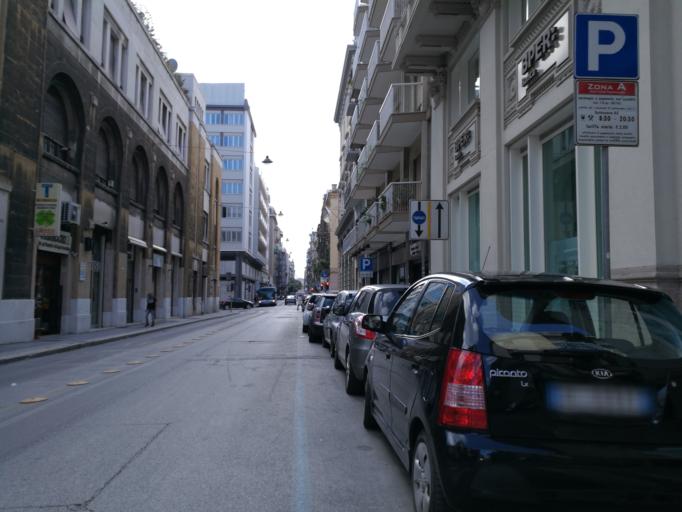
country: IT
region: Apulia
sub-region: Provincia di Bari
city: Bari
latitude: 41.1246
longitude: 16.8686
